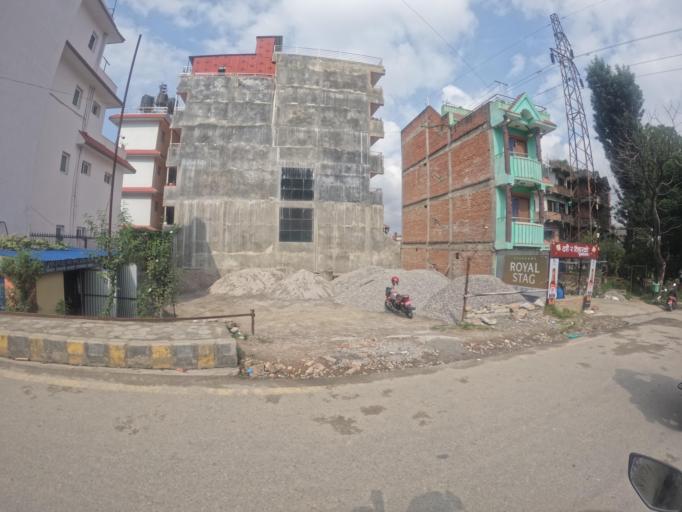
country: NP
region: Central Region
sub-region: Bagmati Zone
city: Bhaktapur
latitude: 27.6670
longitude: 85.3862
